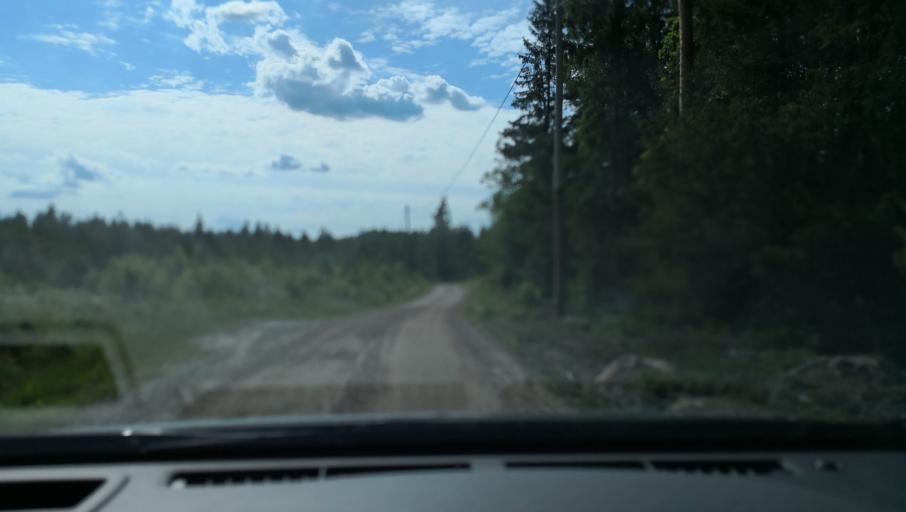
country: SE
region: Uppsala
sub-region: Enkopings Kommun
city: Orsundsbro
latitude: 59.8337
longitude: 17.2413
